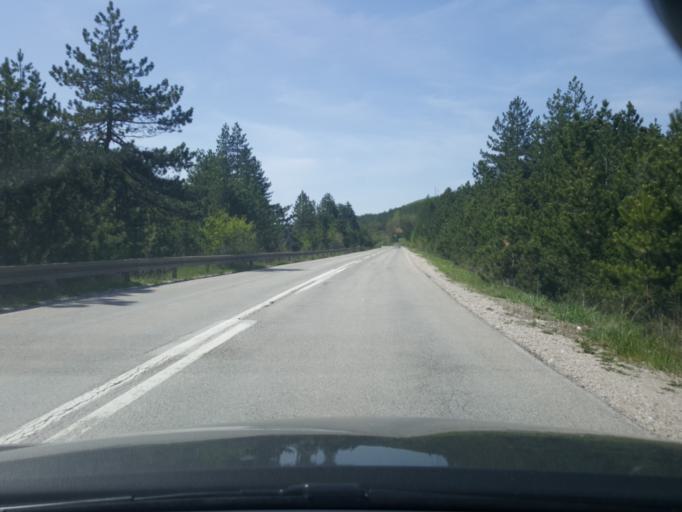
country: RS
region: Central Serbia
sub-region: Zlatiborski Okrug
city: Cajetina
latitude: 43.7870
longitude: 19.6645
